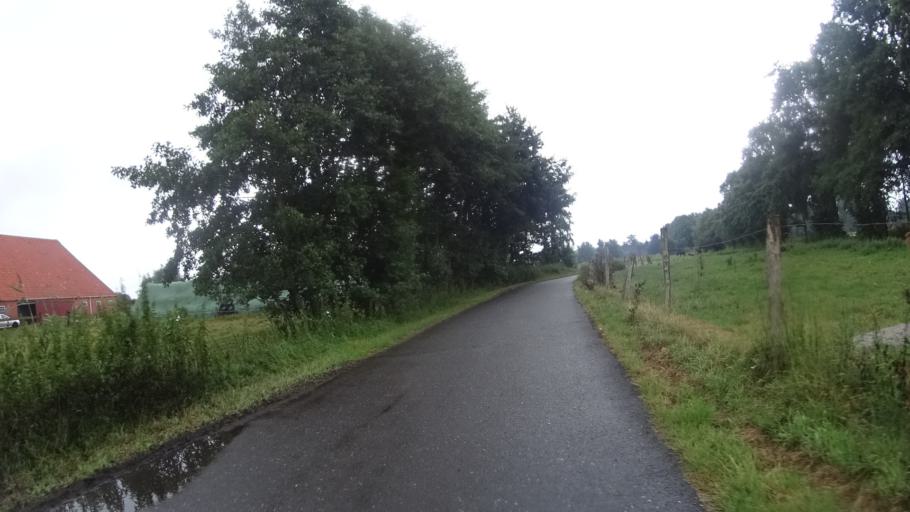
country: DE
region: Lower Saxony
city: Weener
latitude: 53.1818
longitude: 7.3131
